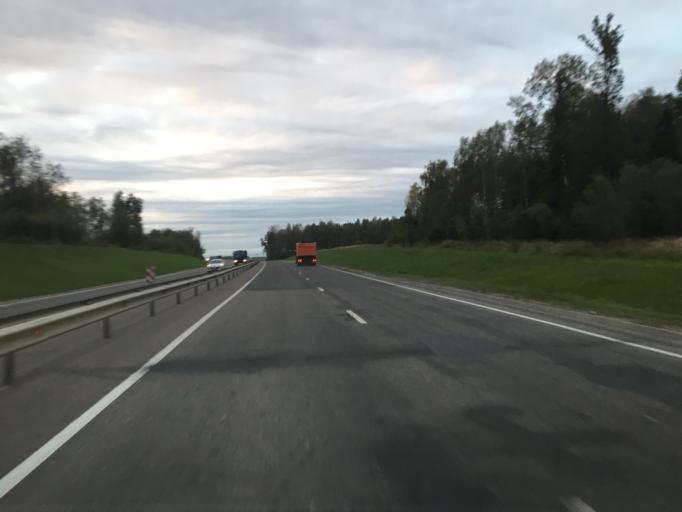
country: RU
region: Kaluga
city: Kaluga
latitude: 54.6089
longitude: 36.3106
